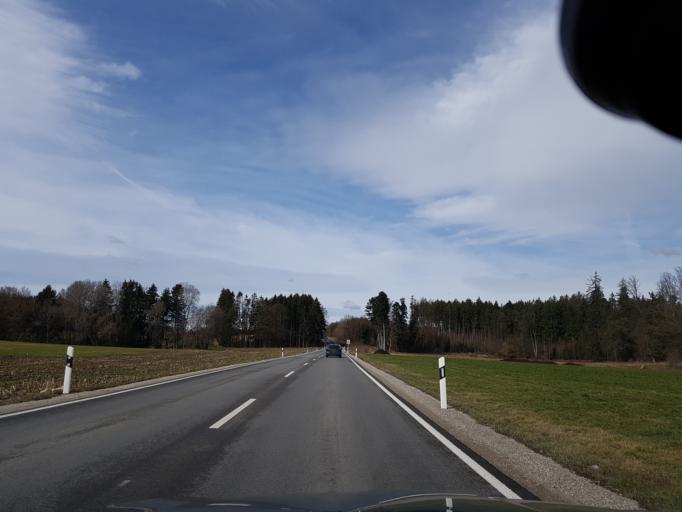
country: DE
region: Bavaria
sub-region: Upper Bavaria
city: Bruckmuhl
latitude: 47.8931
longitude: 11.9001
